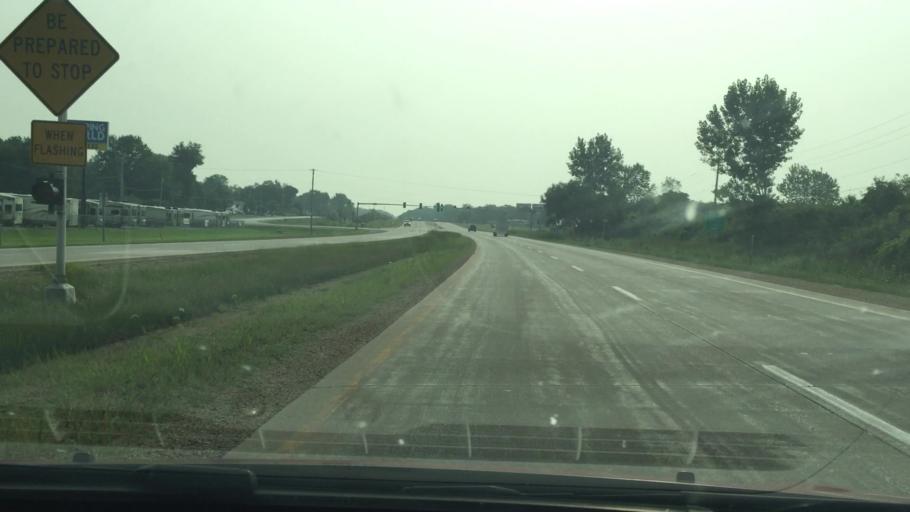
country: US
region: Iowa
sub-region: Scott County
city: Buffalo
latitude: 41.5085
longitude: -90.6911
